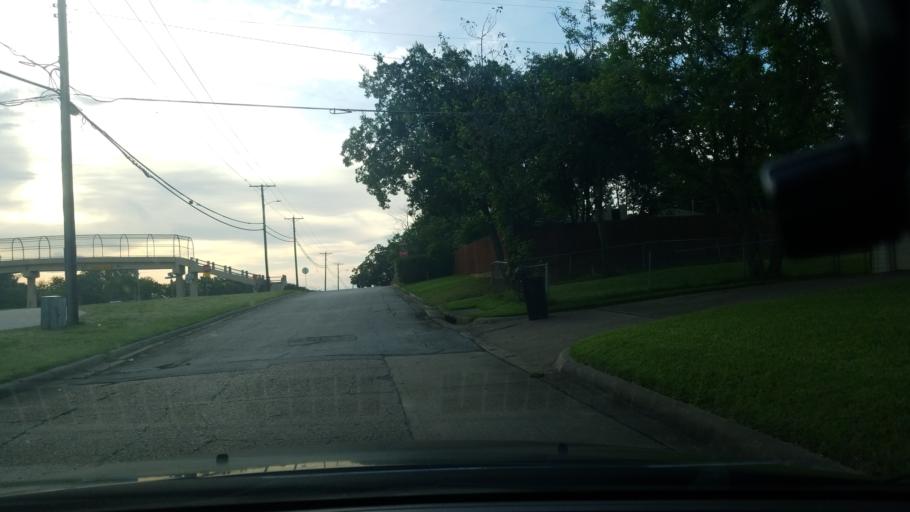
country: US
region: Texas
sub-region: Dallas County
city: Mesquite
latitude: 32.7680
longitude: -96.6364
